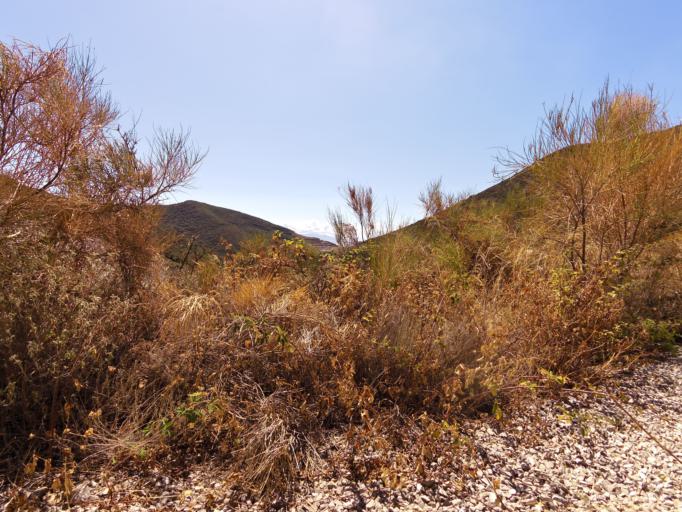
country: IT
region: Tuscany
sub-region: Provincia di Livorno
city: Campiglia Marittima
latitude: 43.0830
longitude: 10.6066
